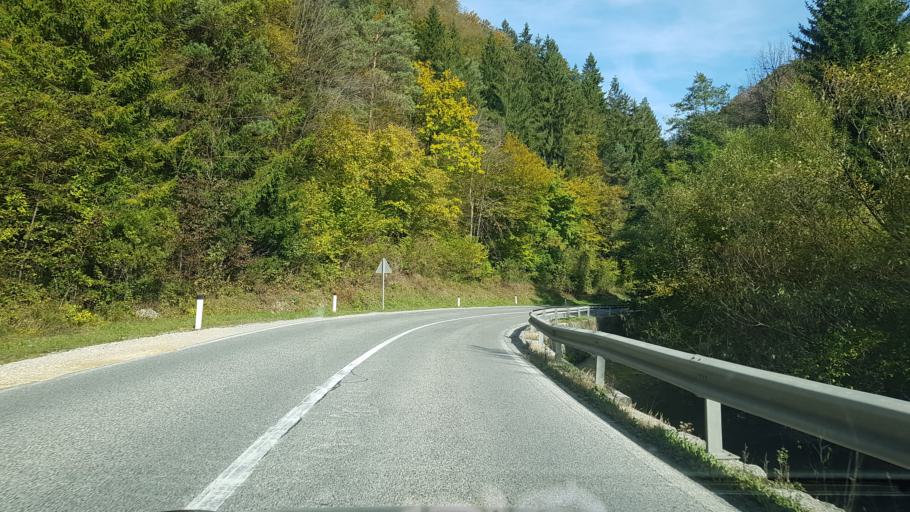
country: SI
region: Velenje
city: Velenje
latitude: 46.3866
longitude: 15.1614
